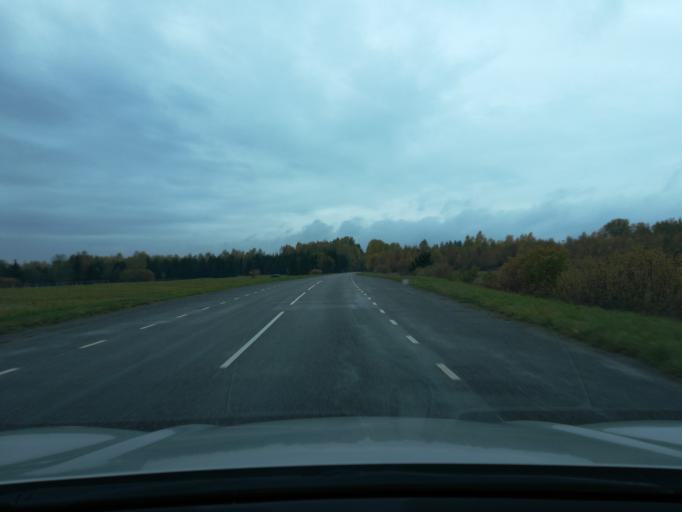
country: EE
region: Ida-Virumaa
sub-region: Johvi vald
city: Johvi
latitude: 59.0744
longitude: 27.3536
